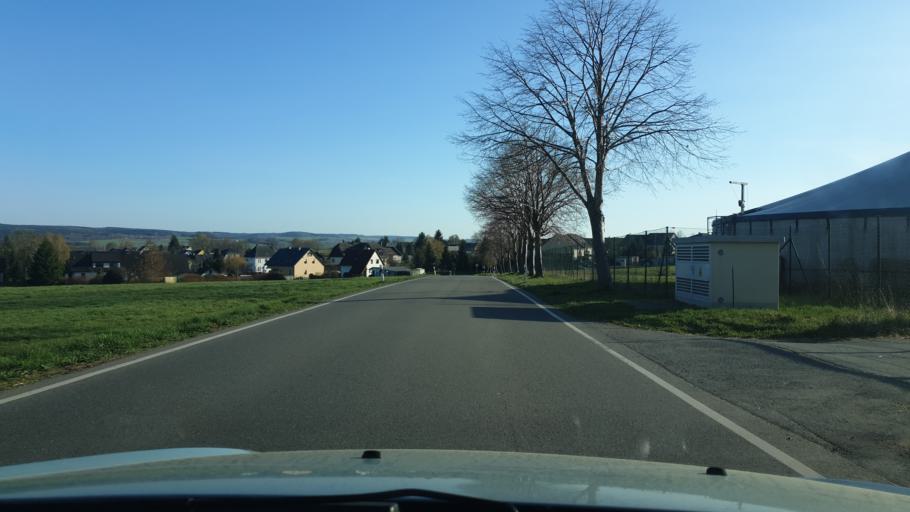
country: DE
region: Saxony
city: Niederdorf
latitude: 50.7678
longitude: 12.8025
